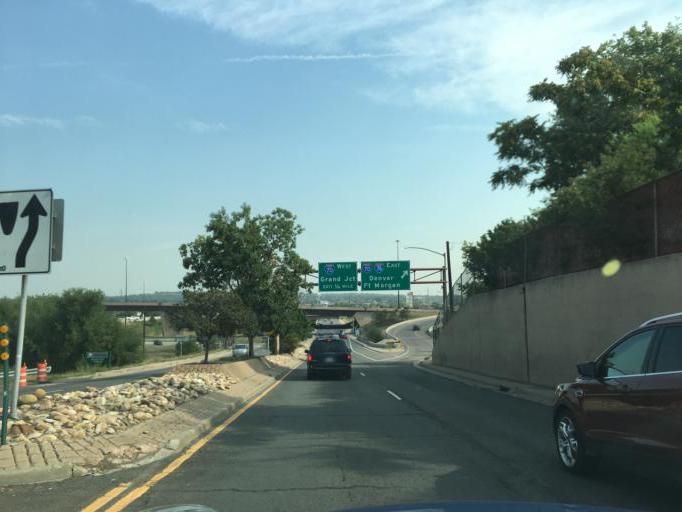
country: US
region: Colorado
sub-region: Jefferson County
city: Wheat Ridge
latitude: 39.7828
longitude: -105.0814
